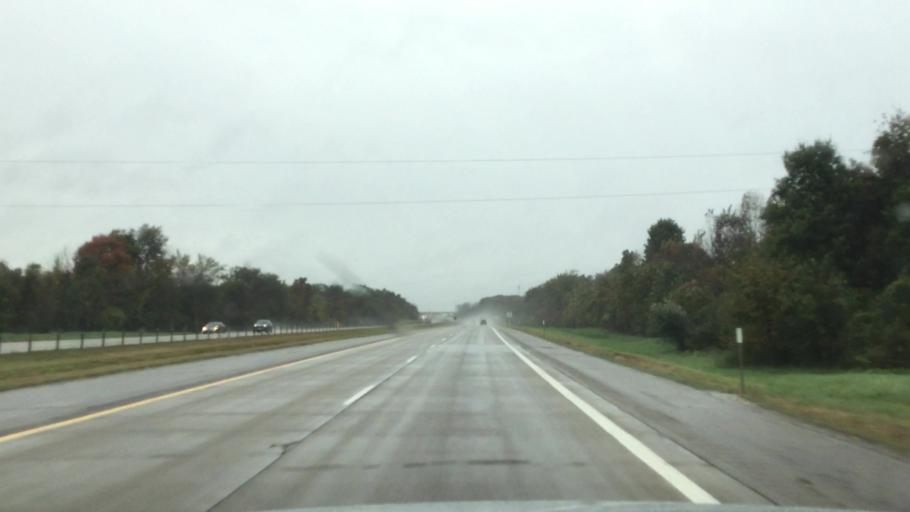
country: US
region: Michigan
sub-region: Berrien County
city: Benton Heights
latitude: 42.1444
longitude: -86.3544
